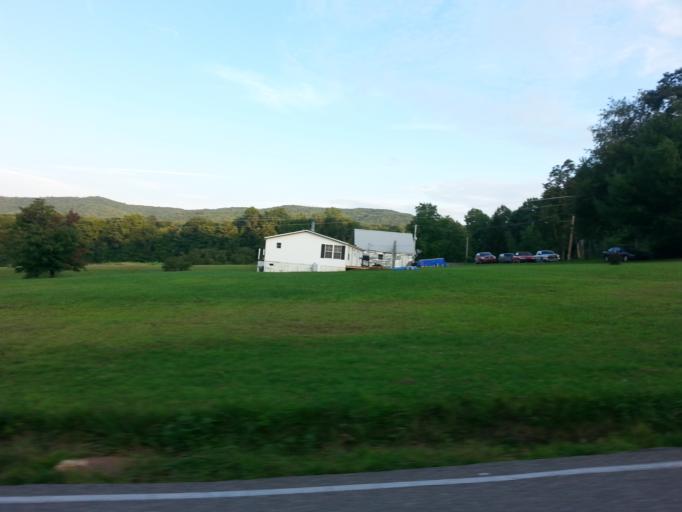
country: US
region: Tennessee
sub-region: Johnson County
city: Mountain City
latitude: 36.4884
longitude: -81.9536
